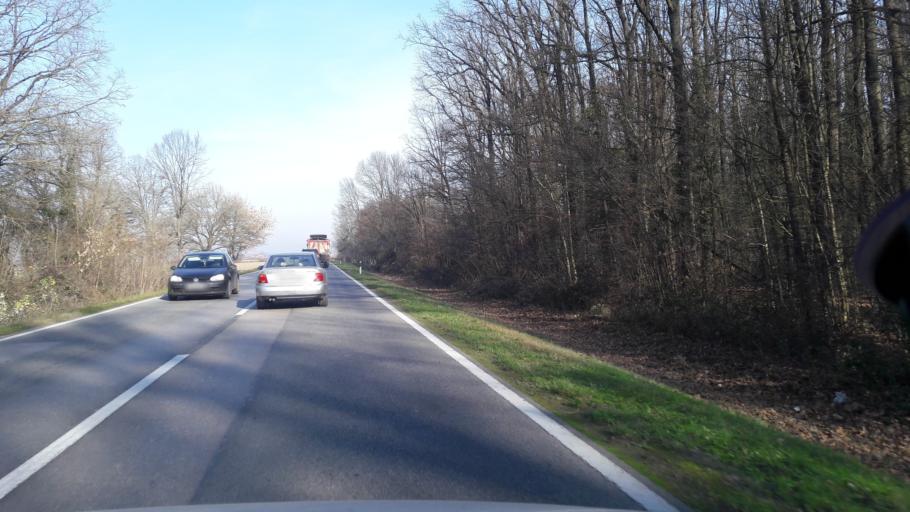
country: HR
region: Vukovarsko-Srijemska
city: Gradiste
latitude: 45.1311
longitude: 18.7178
